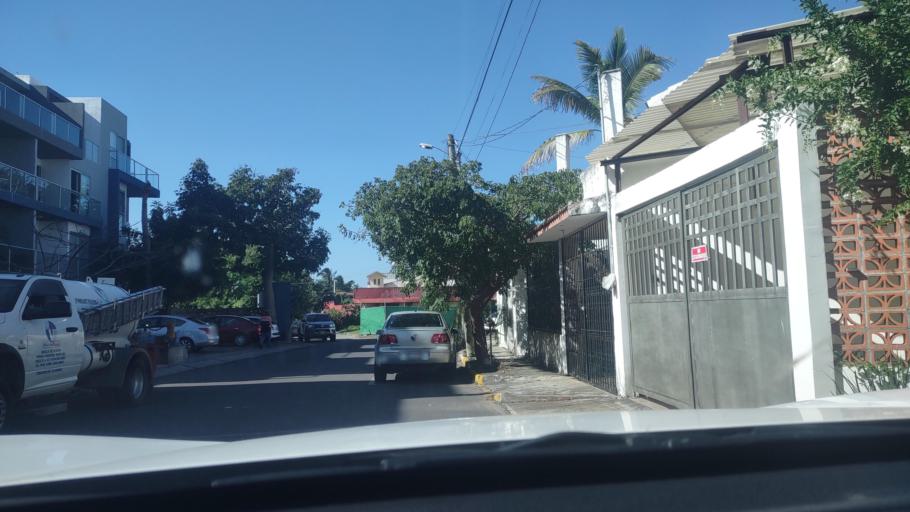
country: MX
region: Veracruz
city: Boca del Rio
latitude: 19.1089
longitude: -96.1127
